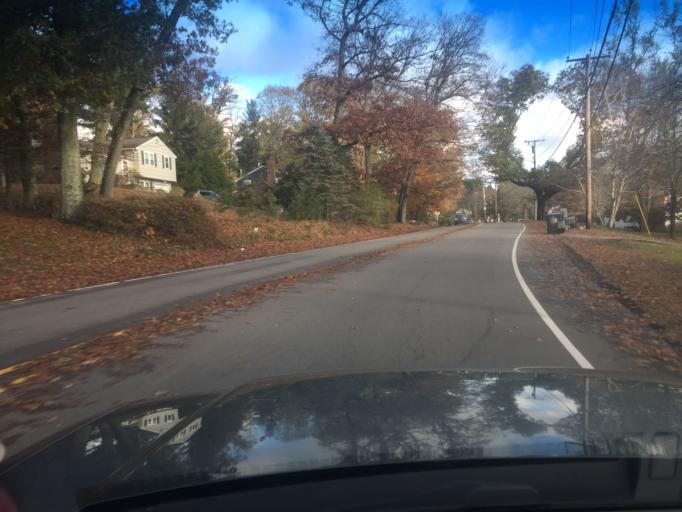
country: US
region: Massachusetts
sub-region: Norfolk County
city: Millis-Clicquot
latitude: 42.1757
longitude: -71.3391
